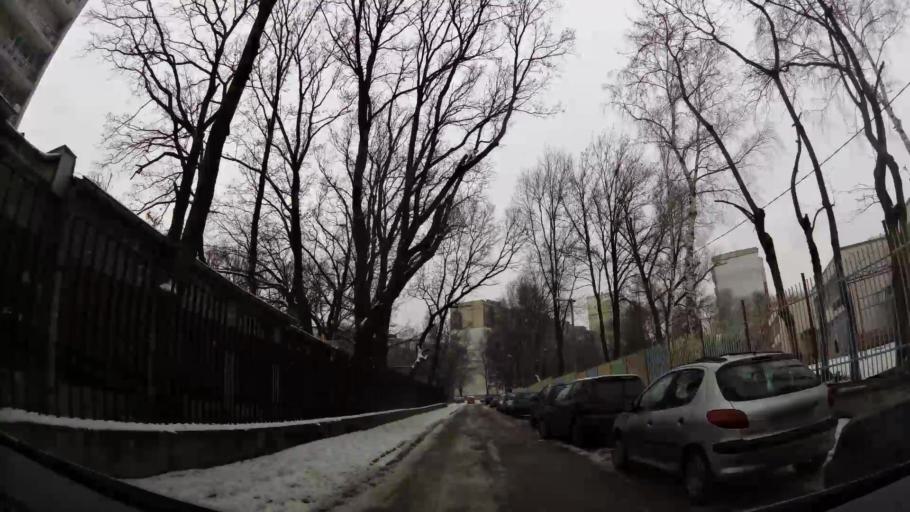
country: BG
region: Sofia-Capital
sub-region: Stolichna Obshtina
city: Sofia
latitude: 42.7135
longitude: 23.3113
